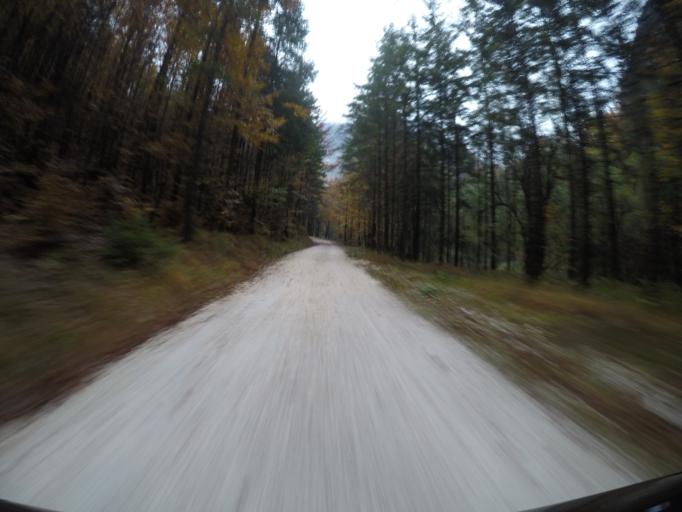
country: SI
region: Kranjska Gora
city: Kranjska Gora
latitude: 46.3832
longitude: 13.7706
